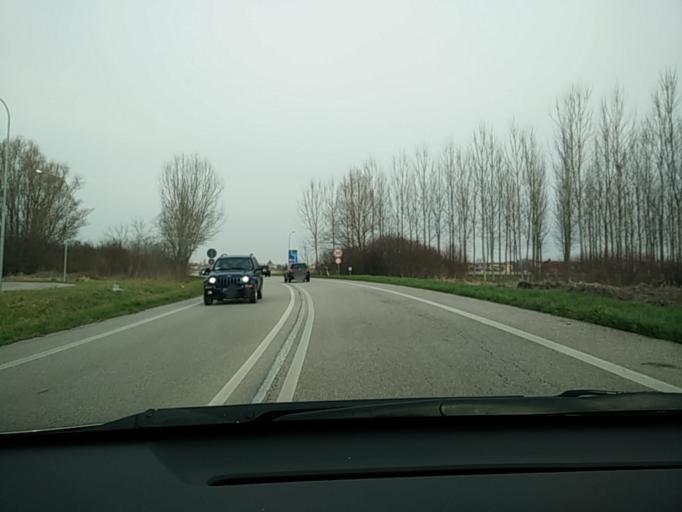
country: IT
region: Veneto
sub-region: Provincia di Venezia
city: San Dona di Piave
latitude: 45.6391
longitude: 12.6021
